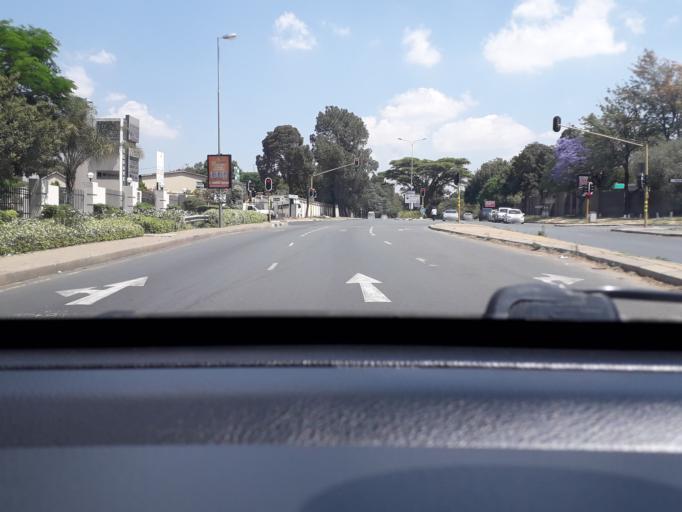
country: ZA
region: Gauteng
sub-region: City of Johannesburg Metropolitan Municipality
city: Modderfontein
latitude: -26.0804
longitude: 28.0625
